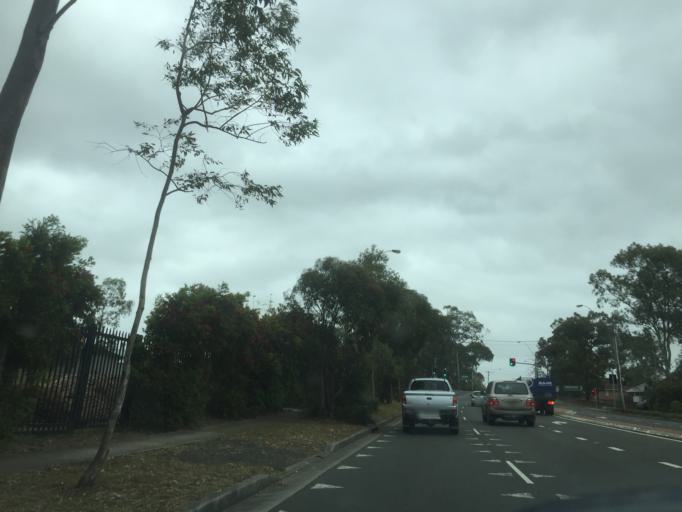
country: AU
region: New South Wales
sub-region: Parramatta
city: Northmead
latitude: -33.7590
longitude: 150.9550
